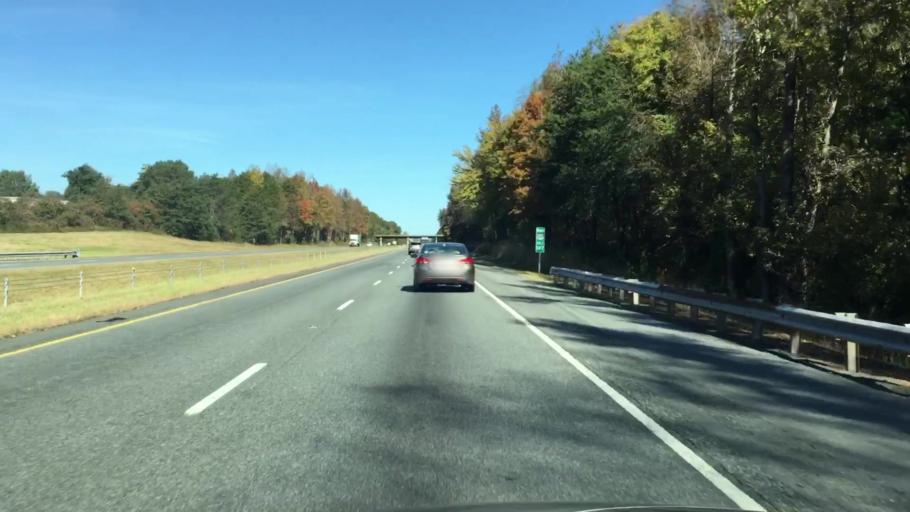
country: US
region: North Carolina
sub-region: Rockingham County
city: Reidsville
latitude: 36.2817
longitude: -79.6400
